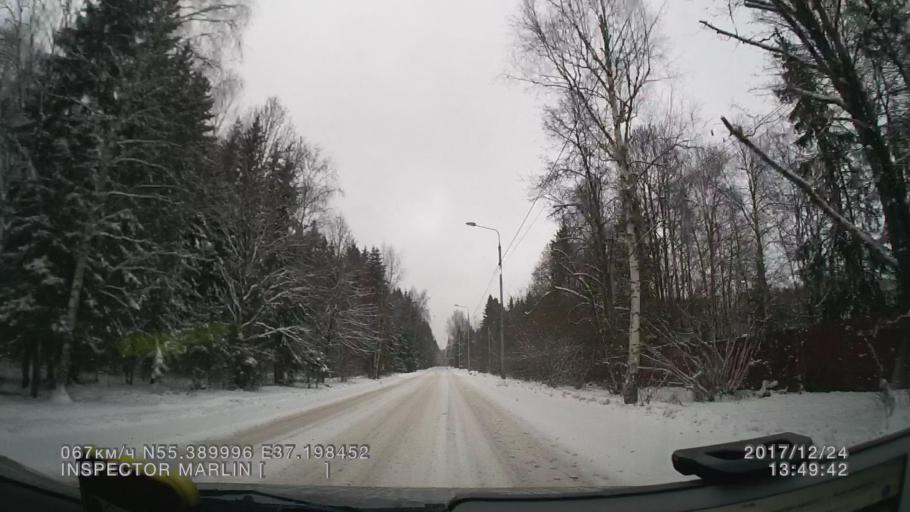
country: RU
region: Moskovskaya
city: Troitsk
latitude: 55.3900
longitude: 37.1984
